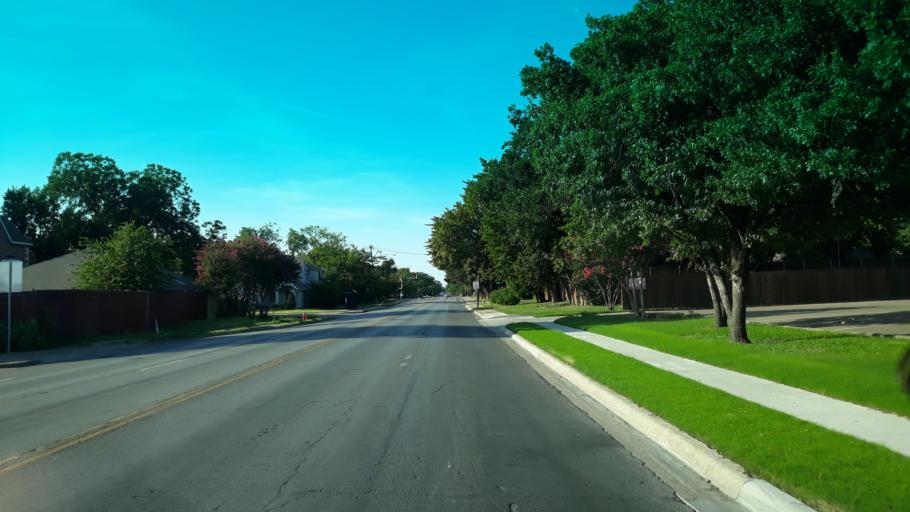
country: US
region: Texas
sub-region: Dallas County
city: Highland Park
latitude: 32.8141
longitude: -96.7615
